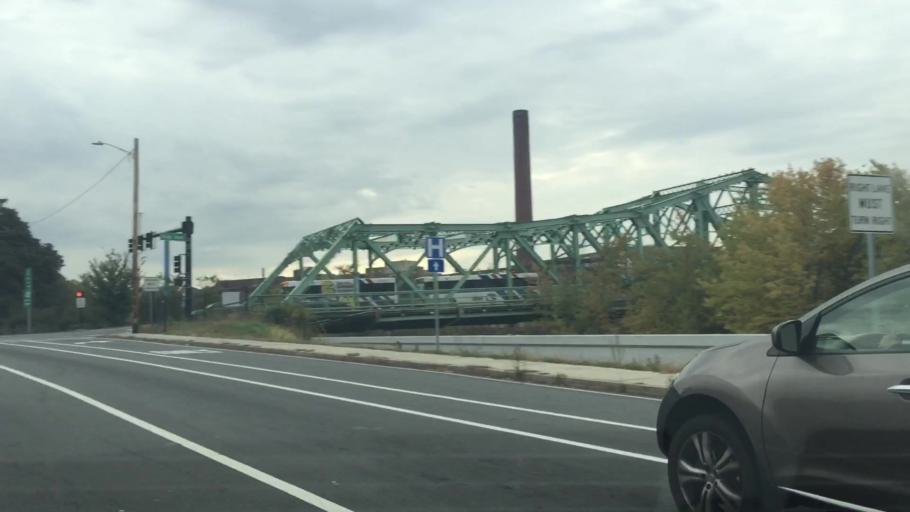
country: US
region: Massachusetts
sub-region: Middlesex County
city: Lowell
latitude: 42.6492
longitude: -71.3052
